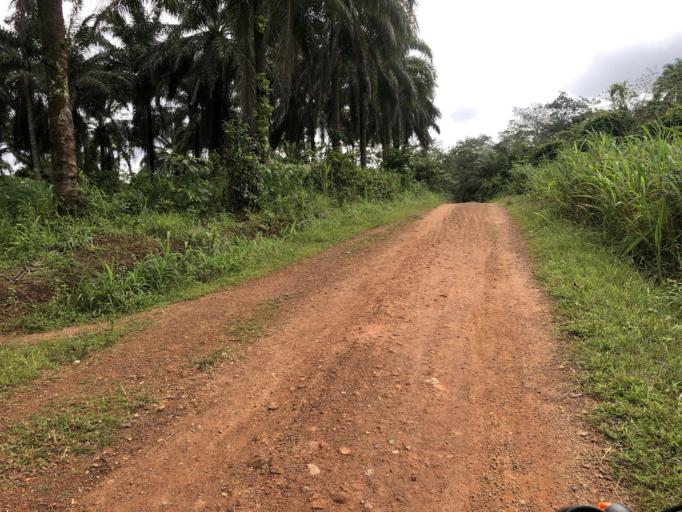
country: SL
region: Eastern Province
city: Kailahun
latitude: 8.2743
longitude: -10.5588
